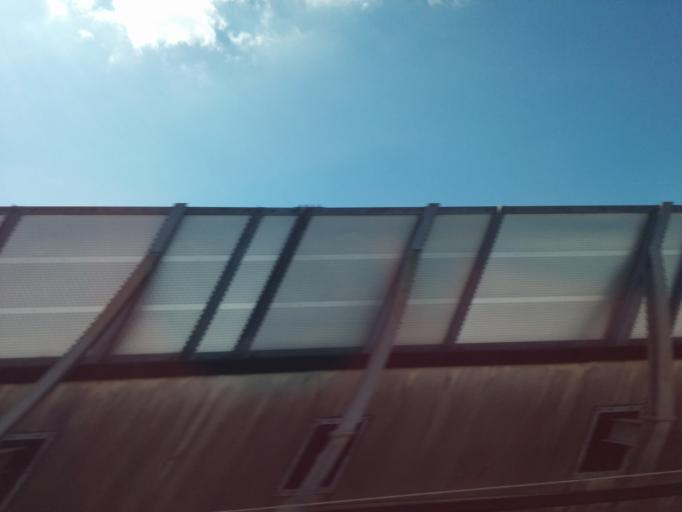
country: JP
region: Aichi
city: Toyohashi
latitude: 34.7317
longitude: 137.4166
